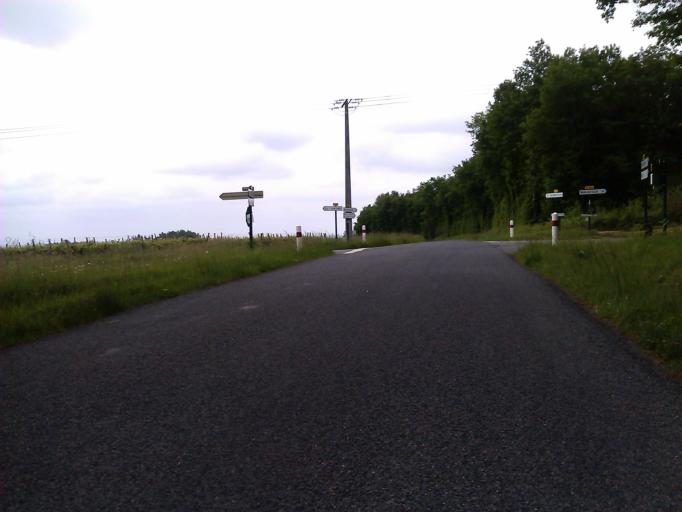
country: FR
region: Poitou-Charentes
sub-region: Departement de la Charente
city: Chateauneuf-sur-Charente
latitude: 45.5443
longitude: -0.0741
